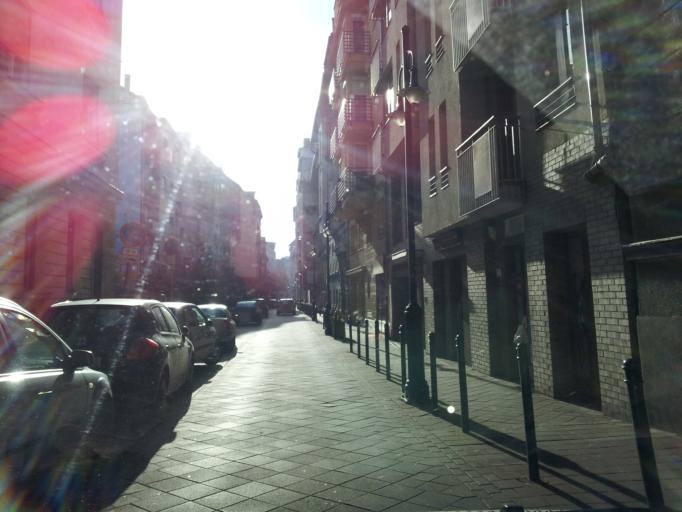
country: HU
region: Budapest
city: Budapest IX. keruelet
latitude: 47.4841
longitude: 19.0705
